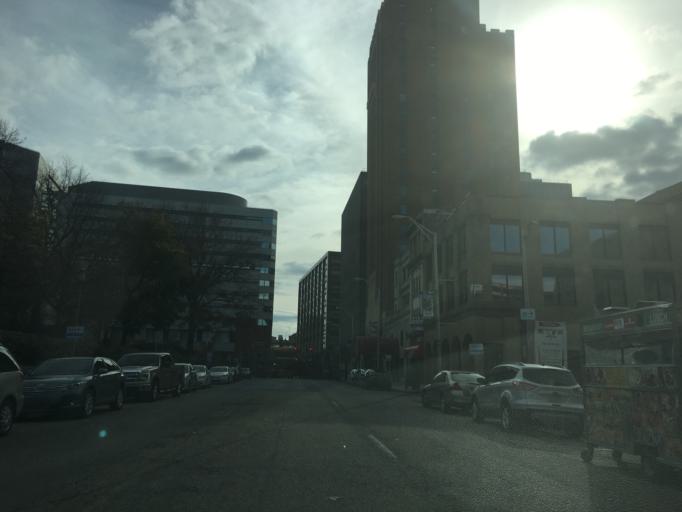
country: US
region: Pennsylvania
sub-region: Dauphin County
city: Harrisburg
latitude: 40.2627
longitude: -76.8837
